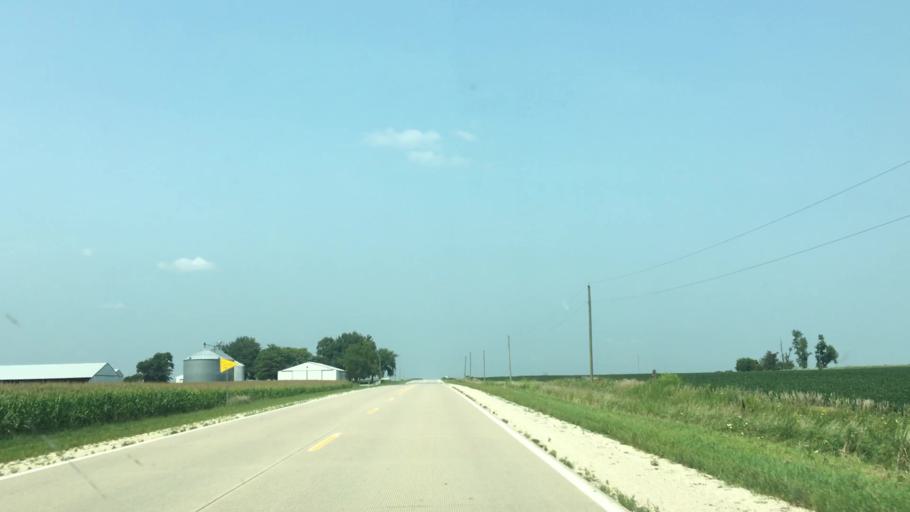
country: US
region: Iowa
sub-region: Fayette County
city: Fayette
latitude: 42.7418
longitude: -91.8041
